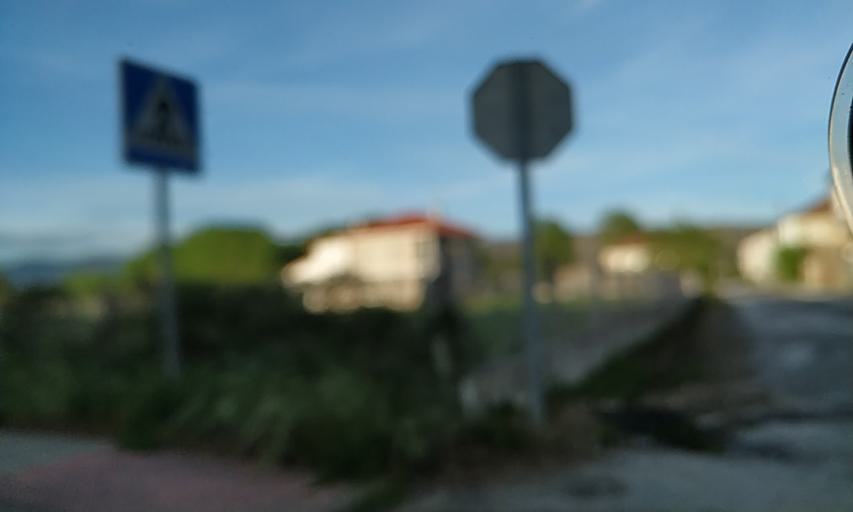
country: ES
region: Galicia
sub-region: Provincia de Ourense
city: Verin
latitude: 41.9211
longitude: -7.4437
